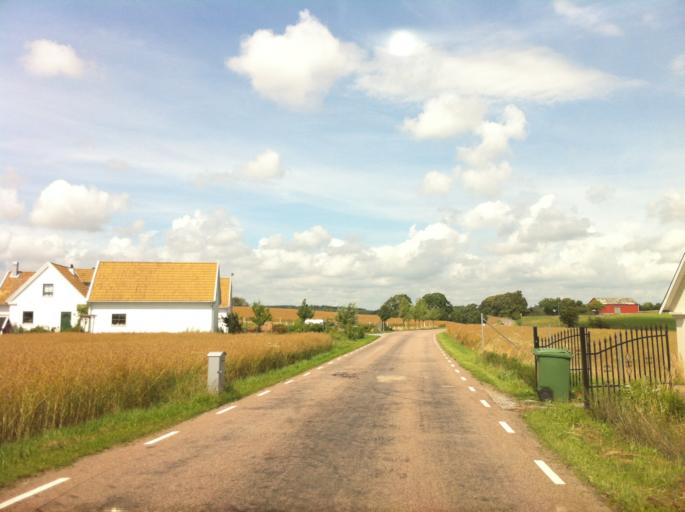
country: SE
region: Skane
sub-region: Skurups Kommun
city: Skurup
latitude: 55.4598
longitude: 13.4290
